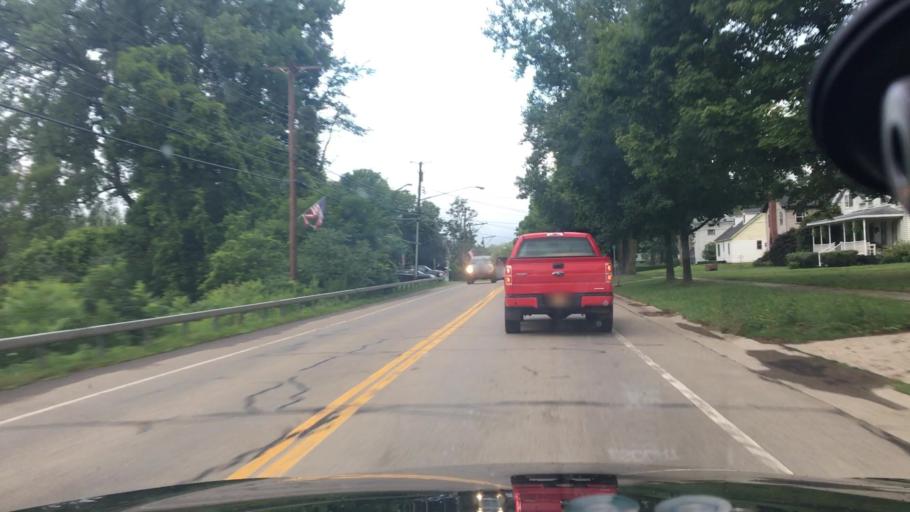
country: US
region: New York
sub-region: Cattaraugus County
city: Randolph
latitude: 42.1702
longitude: -78.9540
